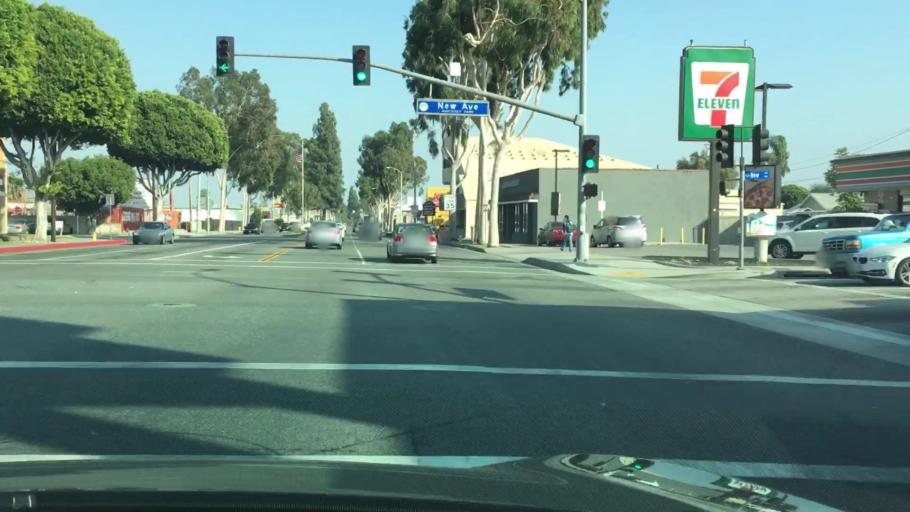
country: US
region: California
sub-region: Los Angeles County
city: Monterey Park
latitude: 34.0625
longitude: -118.1083
